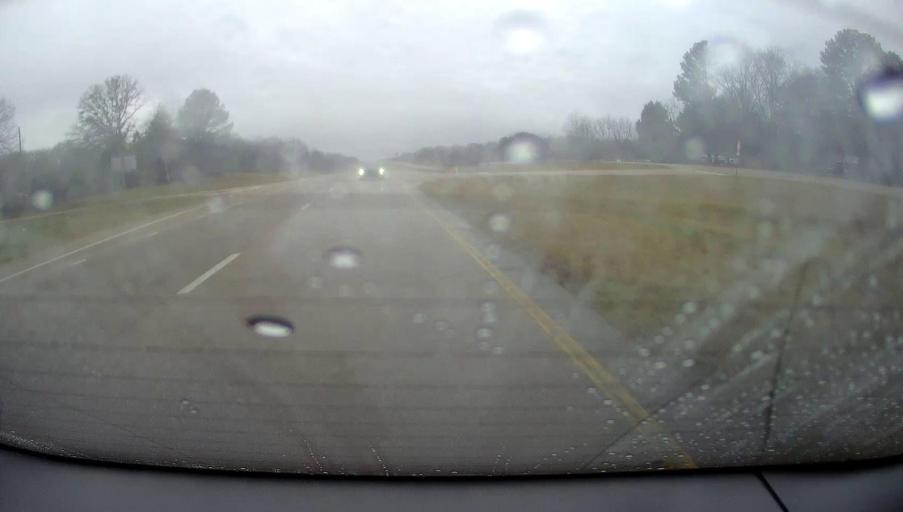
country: US
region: Mississippi
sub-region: Marshall County
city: Holly Springs
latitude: 34.9461
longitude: -89.3523
